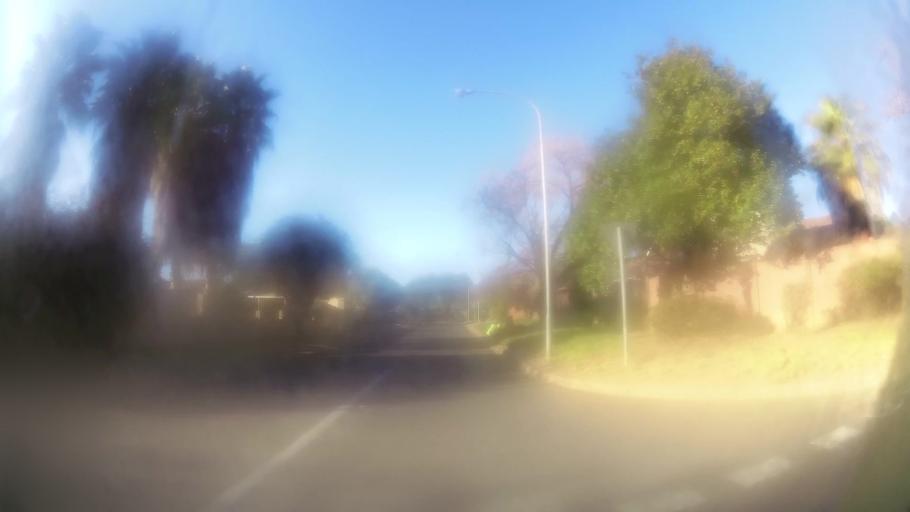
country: ZA
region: Gauteng
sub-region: City of Tshwane Metropolitan Municipality
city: Centurion
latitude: -25.8912
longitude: 28.1319
